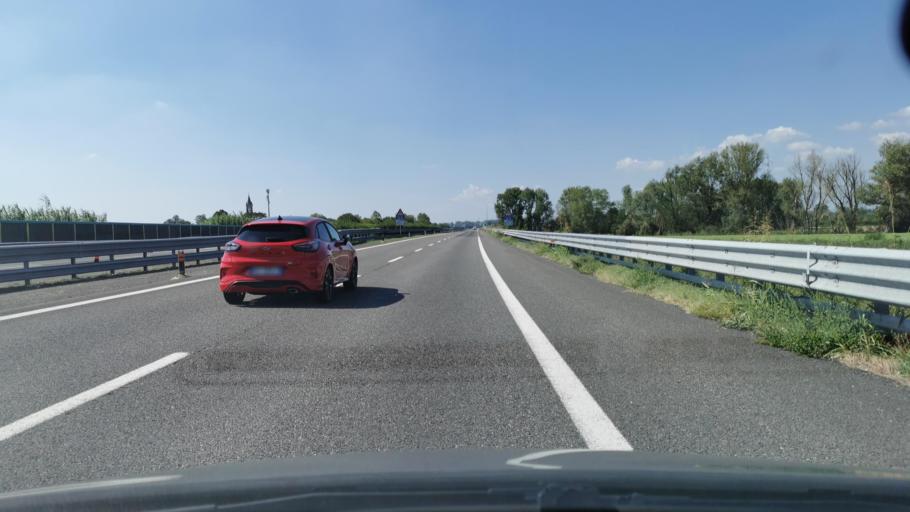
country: IT
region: Emilia-Romagna
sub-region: Provincia di Piacenza
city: Pontenure
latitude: 45.0453
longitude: 9.8062
